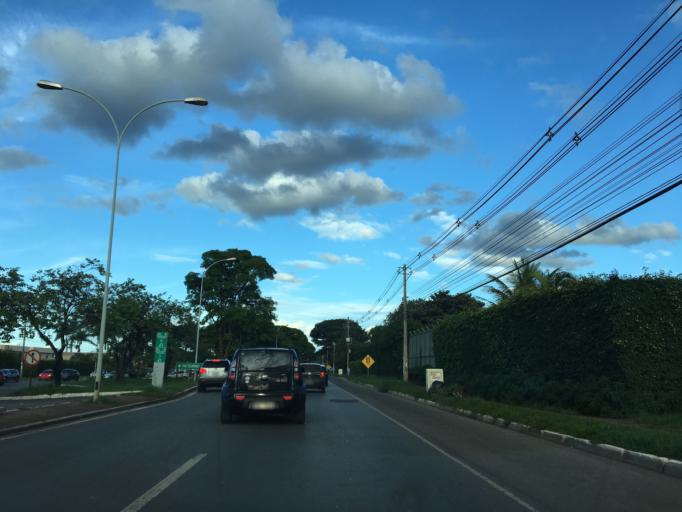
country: BR
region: Federal District
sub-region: Brasilia
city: Brasilia
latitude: -15.8451
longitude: -47.8940
